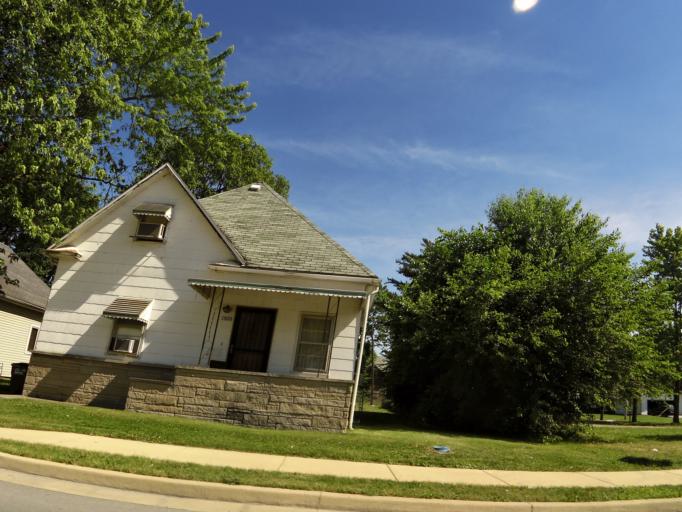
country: US
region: Illinois
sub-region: Vermilion County
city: Danville
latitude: 40.1323
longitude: -87.5799
